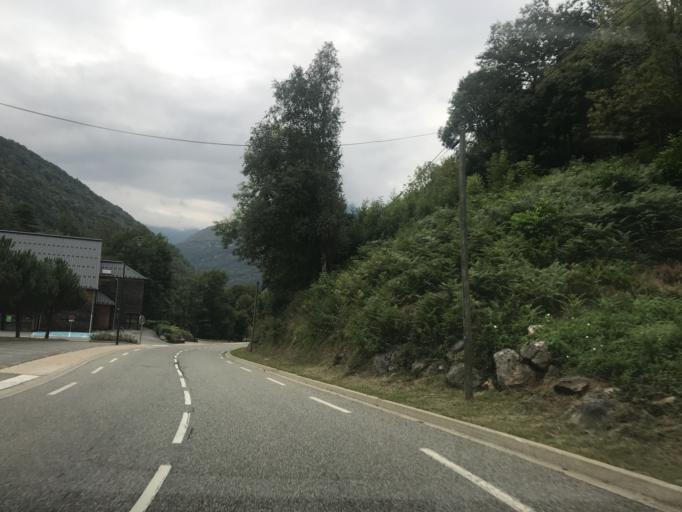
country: FR
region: Midi-Pyrenees
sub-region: Departement de la Haute-Garonne
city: Bagneres-de-Luchon
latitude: 42.7731
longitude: 0.6065
